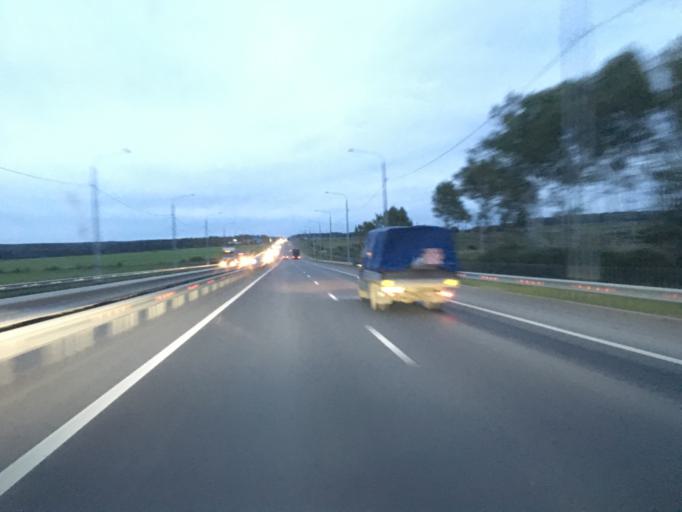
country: RU
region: Kaluga
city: Maloyaroslavets
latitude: 54.9474
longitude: 36.4412
